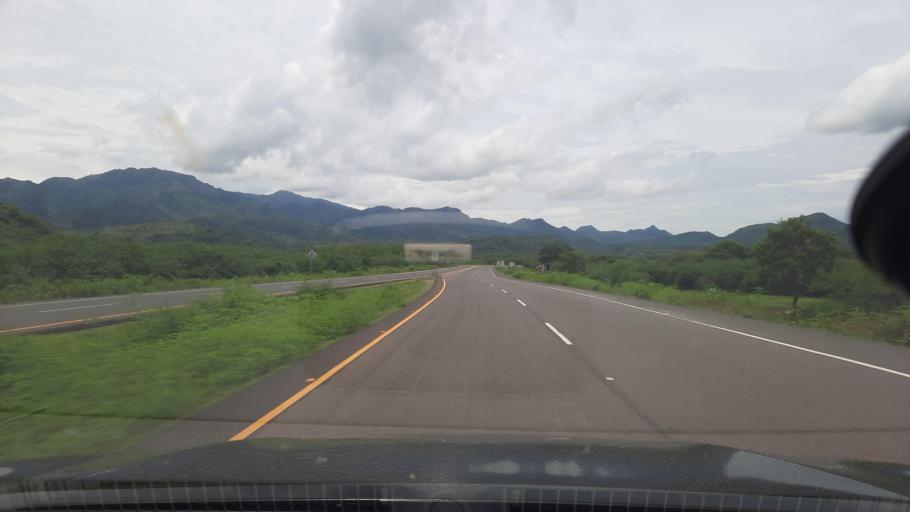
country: HN
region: Valle
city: Aramecina
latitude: 13.7284
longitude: -87.7156
